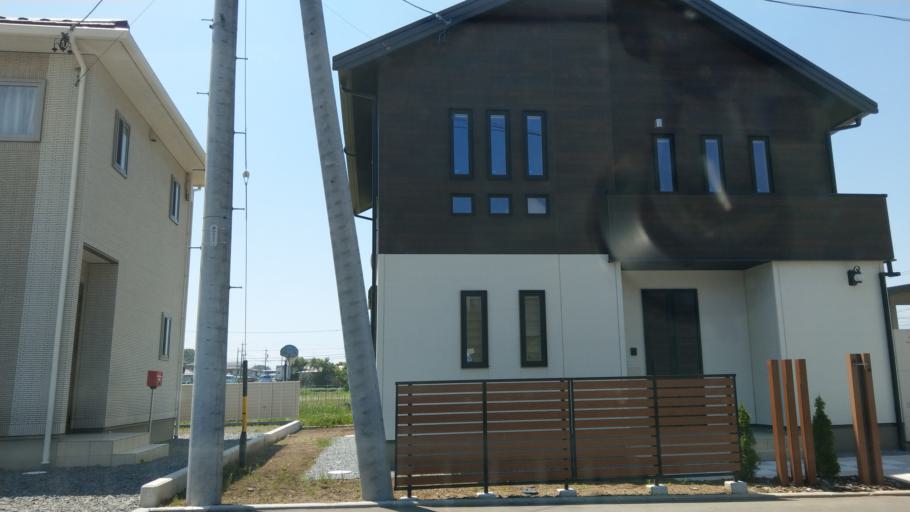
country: JP
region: Nagano
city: Komoro
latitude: 36.3002
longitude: 138.4547
